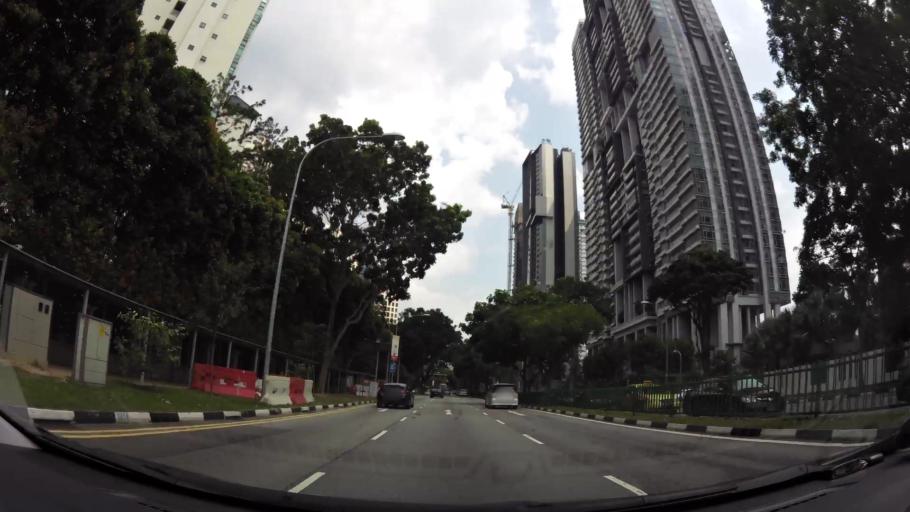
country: SG
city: Singapore
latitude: 1.2915
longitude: 103.8161
